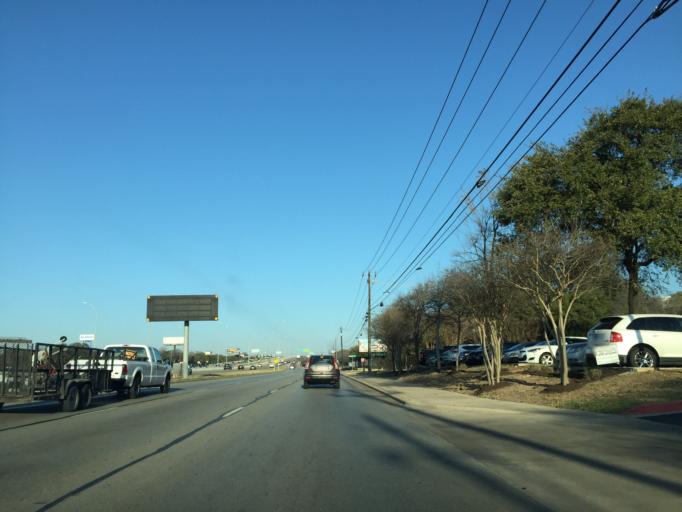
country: US
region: Texas
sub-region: Williamson County
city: Jollyville
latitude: 30.4261
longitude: -97.7520
